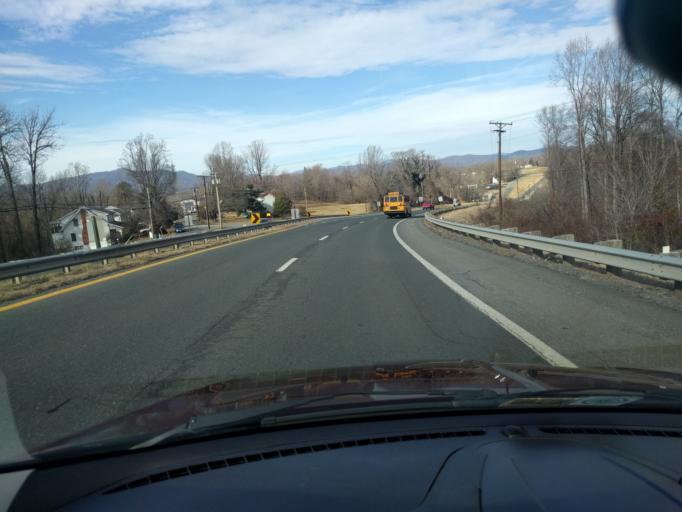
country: US
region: Virginia
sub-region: Amherst County
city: Madison Heights
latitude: 37.4942
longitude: -79.1253
